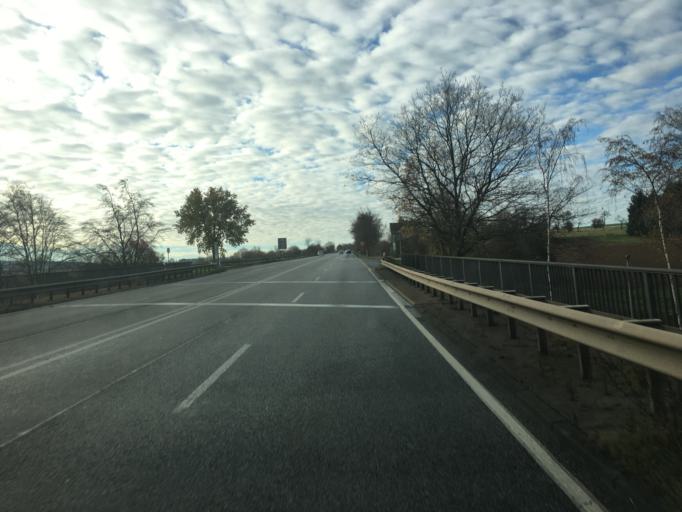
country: DE
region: North Rhine-Westphalia
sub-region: Regierungsbezirk Koln
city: Kall
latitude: 50.5638
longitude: 6.5803
